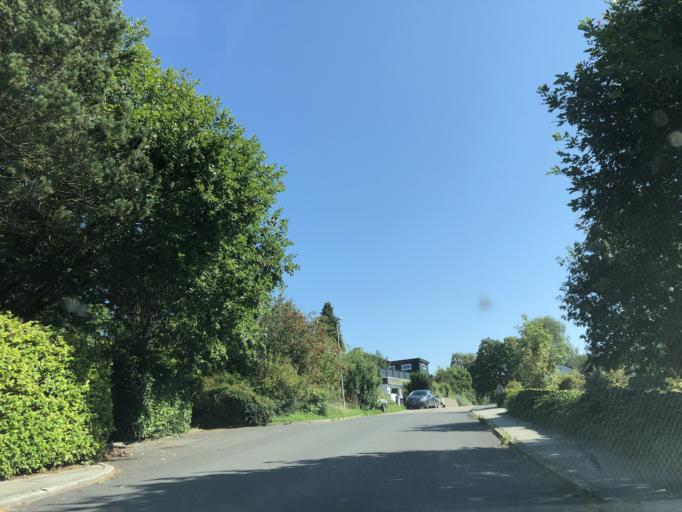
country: DK
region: Central Jutland
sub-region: Silkeborg Kommune
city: Silkeborg
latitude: 56.1910
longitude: 9.5841
